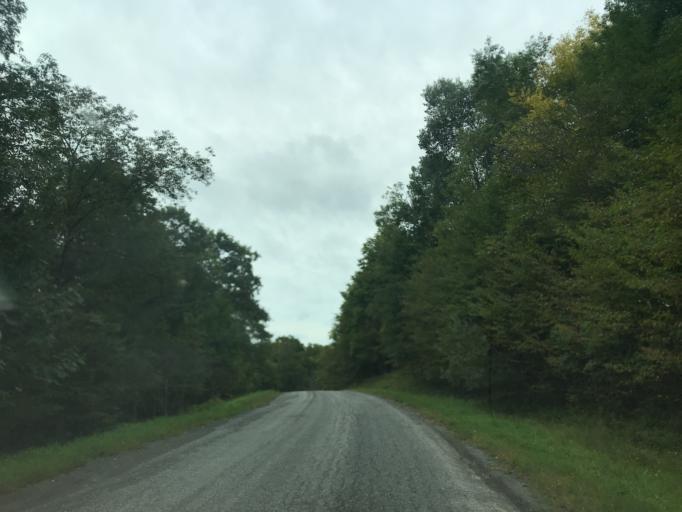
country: US
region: New York
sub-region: Otsego County
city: Worcester
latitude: 42.5155
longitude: -74.6625
